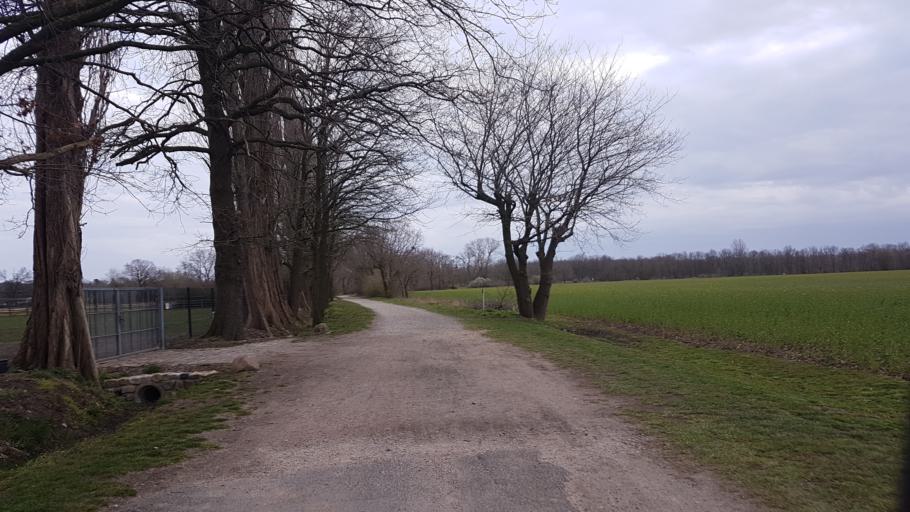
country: DE
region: Lower Saxony
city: Langenhagen
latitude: 52.4441
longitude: 9.7871
